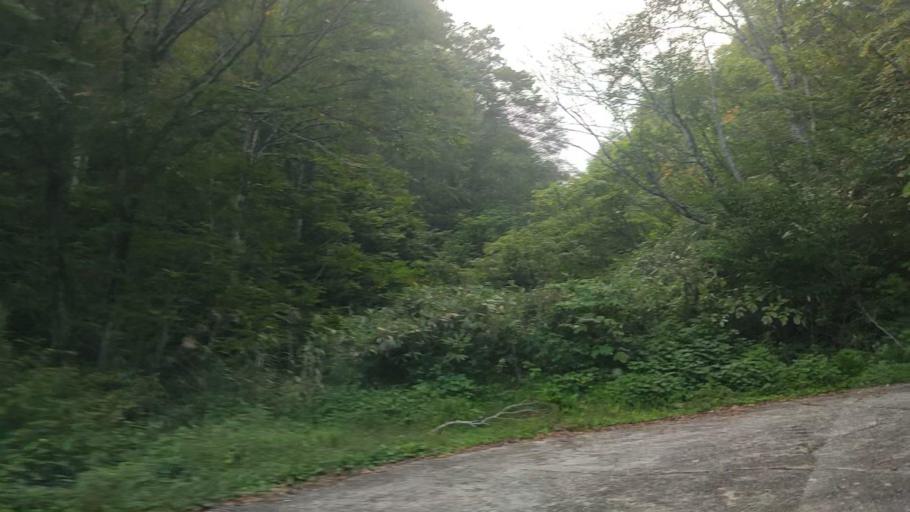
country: JP
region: Toyama
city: Yatsuomachi-higashikumisaka
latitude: 36.3455
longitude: 137.0695
